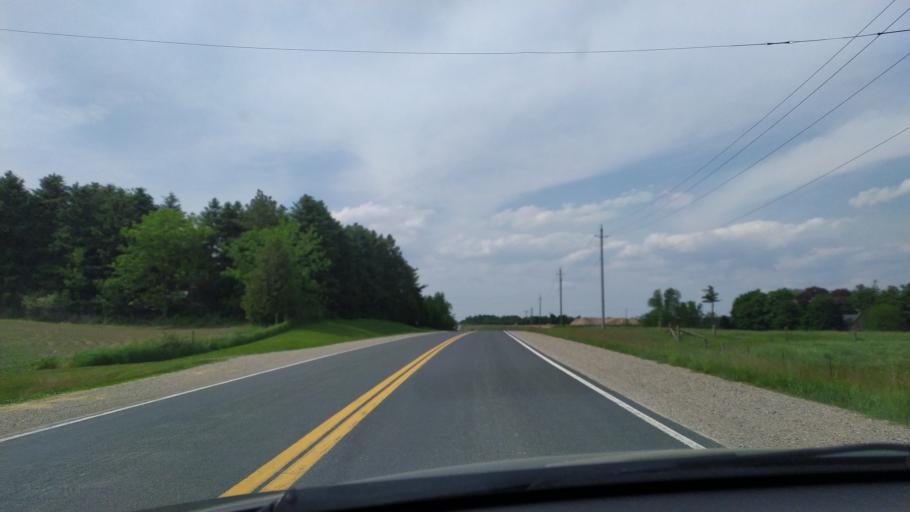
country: CA
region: Ontario
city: Ingersoll
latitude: 43.0112
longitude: -80.9634
